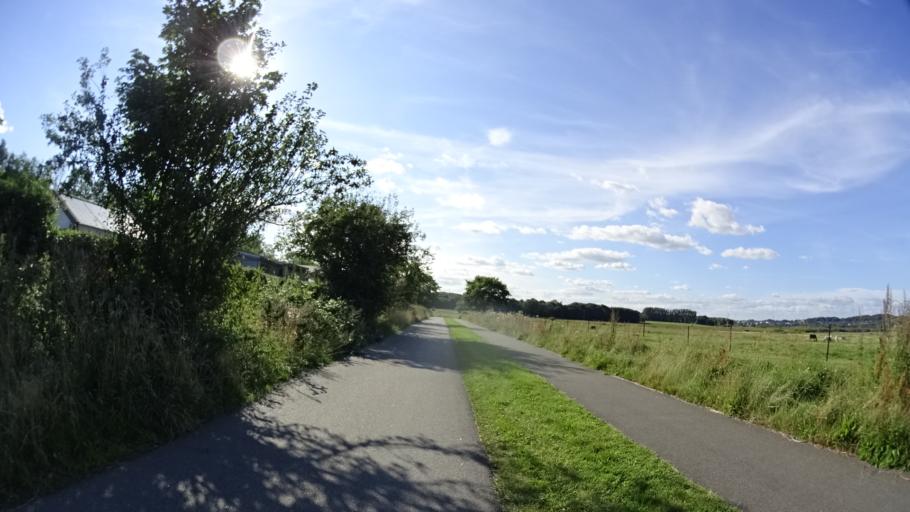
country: DK
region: Central Jutland
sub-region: Arhus Kommune
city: Stavtrup
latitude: 56.1342
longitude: 10.1394
